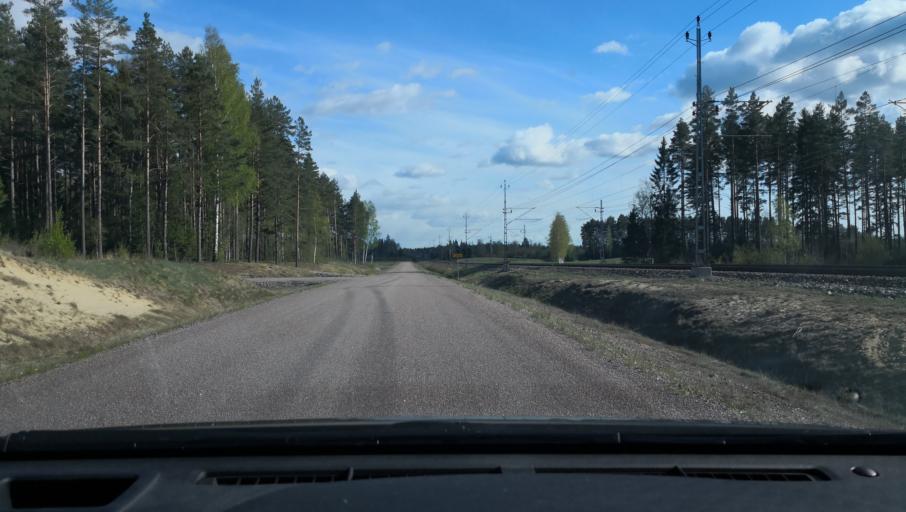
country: SE
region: OErebro
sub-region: Askersunds Kommun
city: Asbro
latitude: 58.9367
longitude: 15.0426
